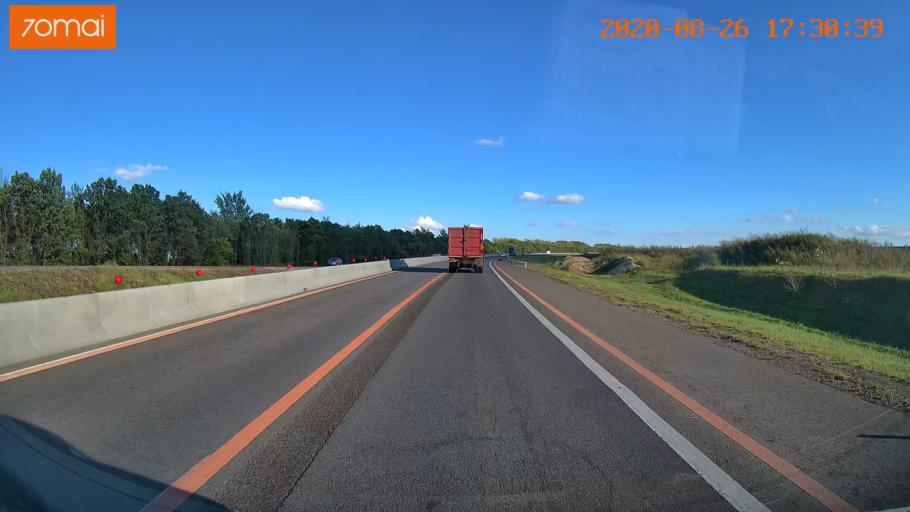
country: RU
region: Tula
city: Kazachka
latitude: 53.4429
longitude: 38.1726
